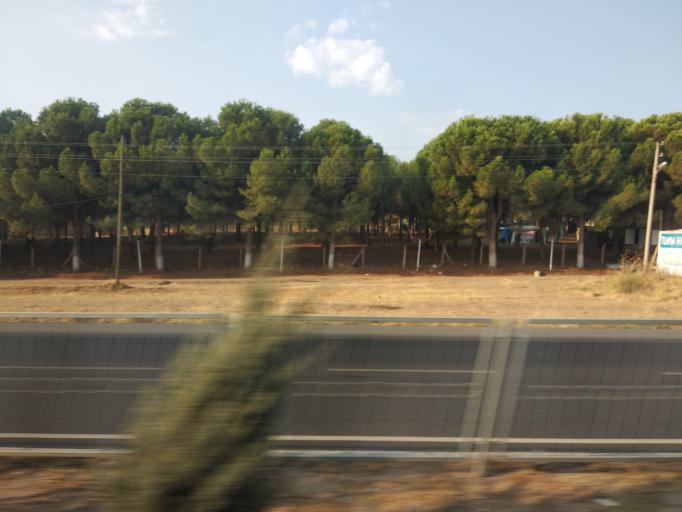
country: TR
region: Manisa
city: Ahmetli
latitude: 38.5049
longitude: 28.0051
